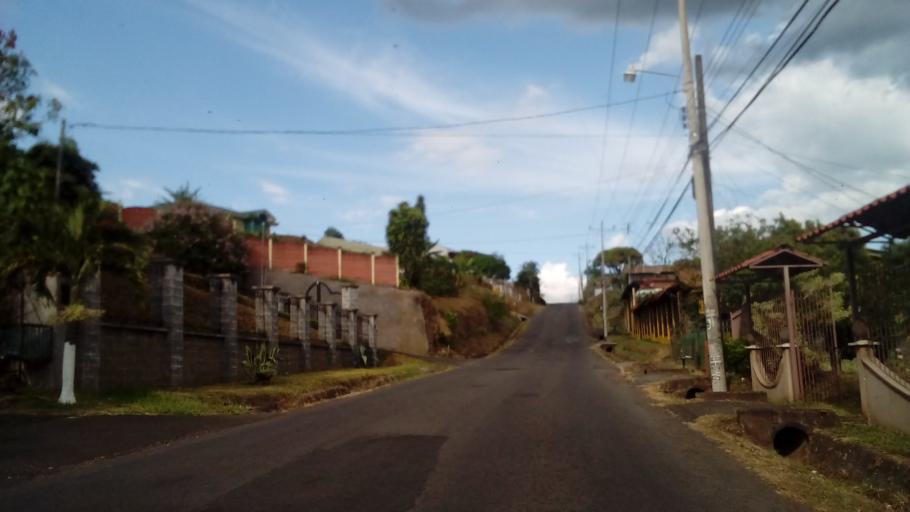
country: CR
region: Alajuela
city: Sabanilla
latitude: 10.0870
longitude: -84.2612
